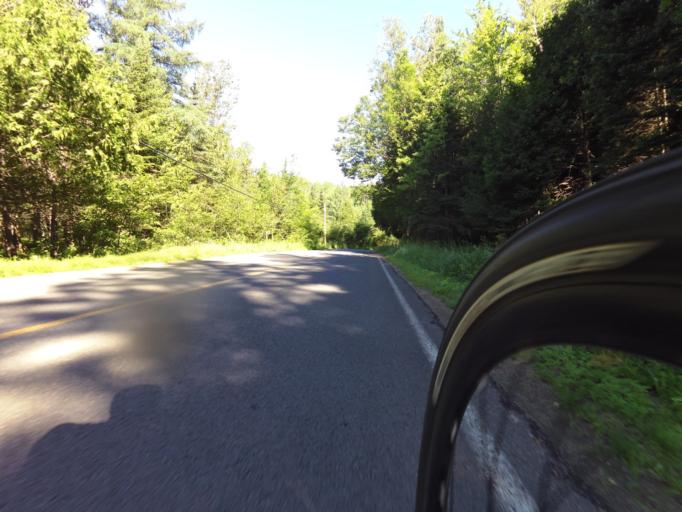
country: CA
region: Quebec
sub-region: Laurentides
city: Brownsburg-Chatham
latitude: 45.8977
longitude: -74.6038
